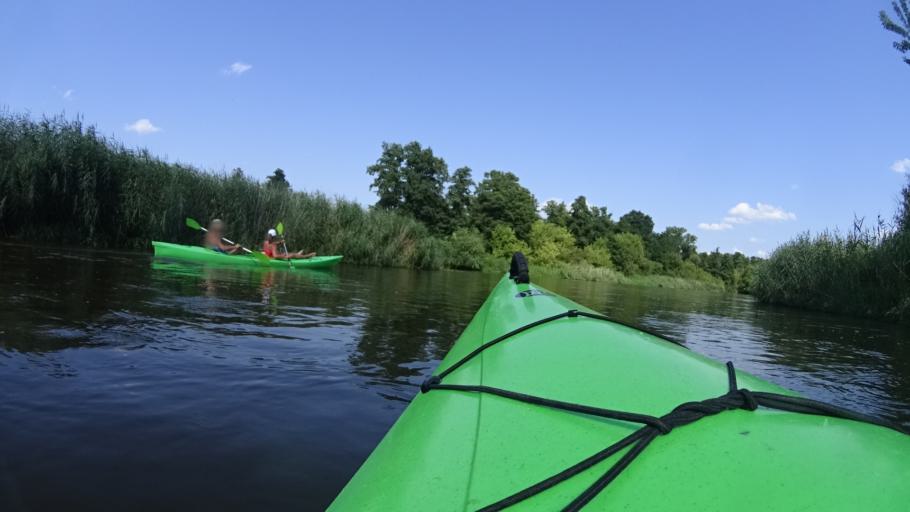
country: PL
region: Masovian Voivodeship
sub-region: Powiat bialobrzeski
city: Bialobrzegi
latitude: 51.6635
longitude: 20.8983
